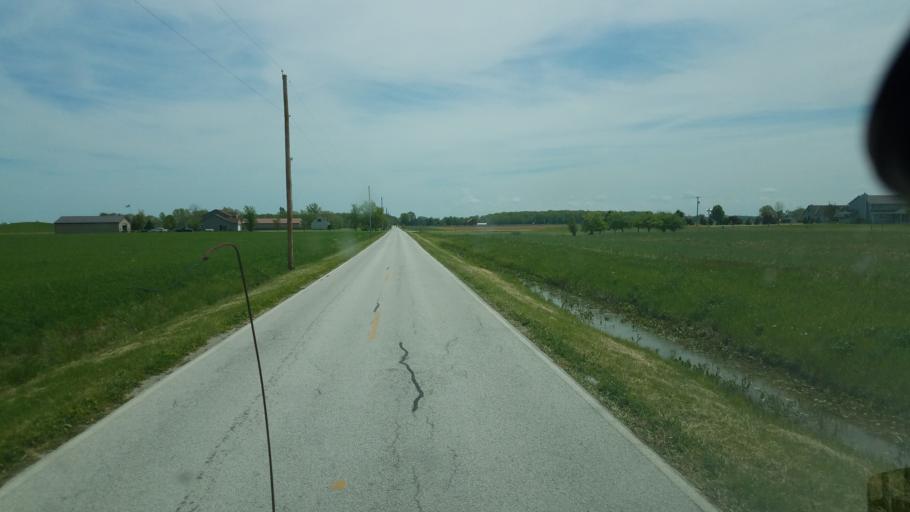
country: US
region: Ohio
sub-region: Ottawa County
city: Oak Harbor
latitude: 41.4869
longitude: -83.1578
